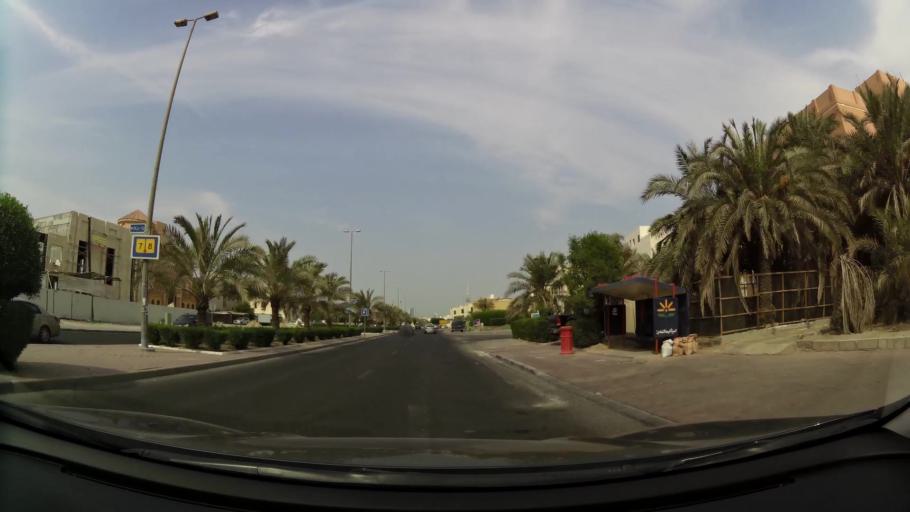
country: KW
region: Al Asimah
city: Ash Shamiyah
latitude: 29.3345
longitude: 47.9772
